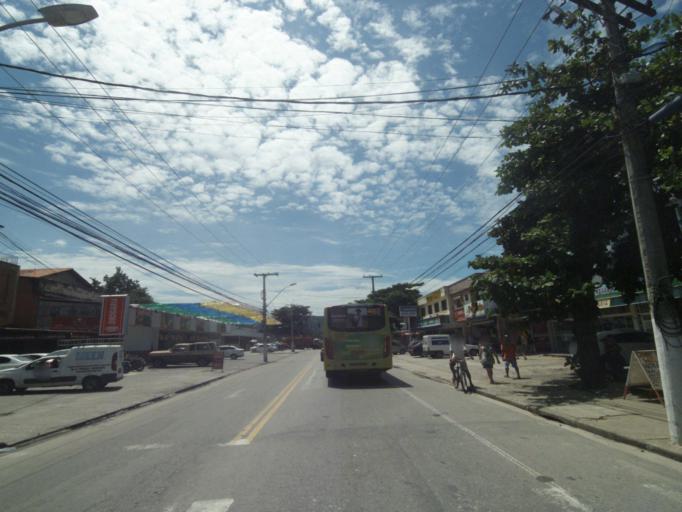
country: BR
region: Rio de Janeiro
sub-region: Niteroi
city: Niteroi
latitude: -22.9437
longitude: -43.0301
